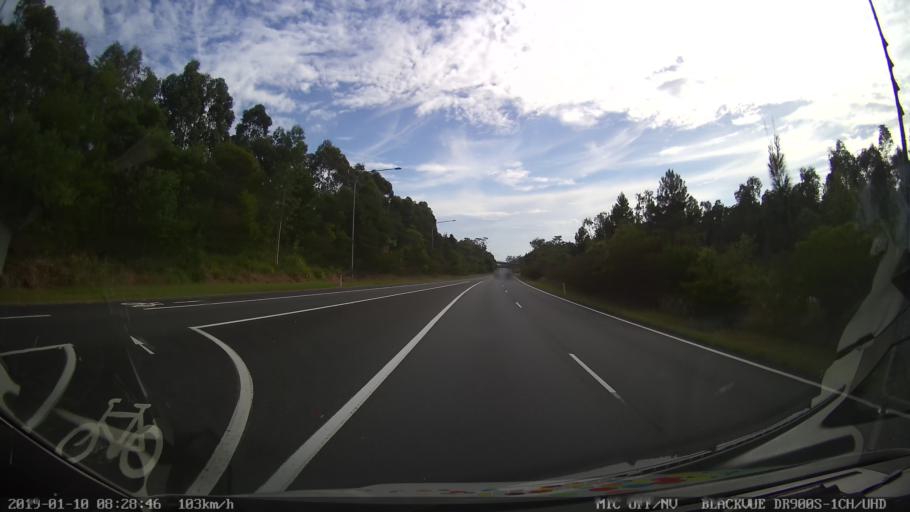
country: AU
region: New South Wales
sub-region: Coffs Harbour
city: Bonville
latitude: -30.3894
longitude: 153.0364
